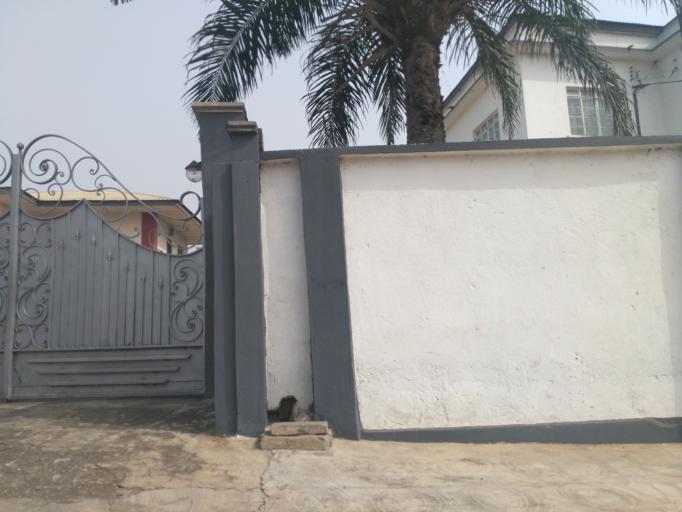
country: GH
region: Ashanti
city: Kumasi
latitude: 6.6799
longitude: -1.6058
